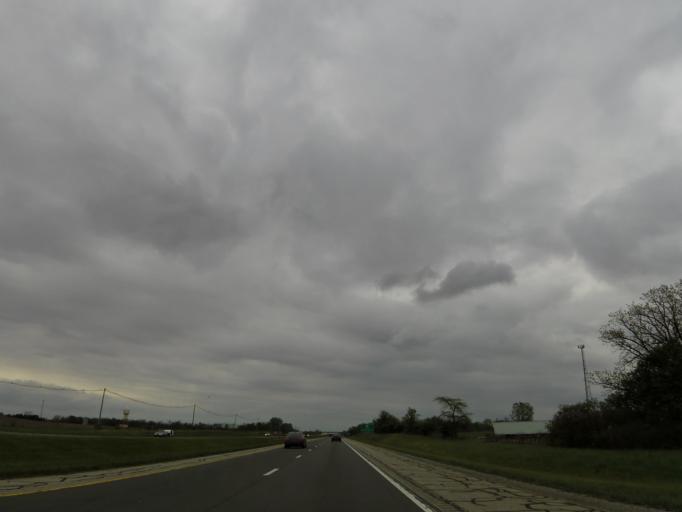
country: US
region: Ohio
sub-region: Madison County
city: Bethel
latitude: 39.6904
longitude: -83.4696
